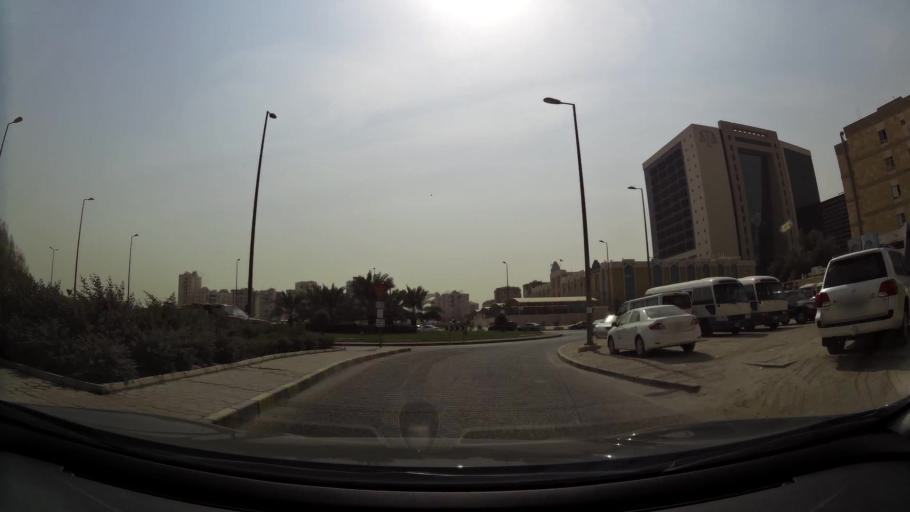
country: KW
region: Al Asimah
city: Ar Rabiyah
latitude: 29.3058
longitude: 47.9149
